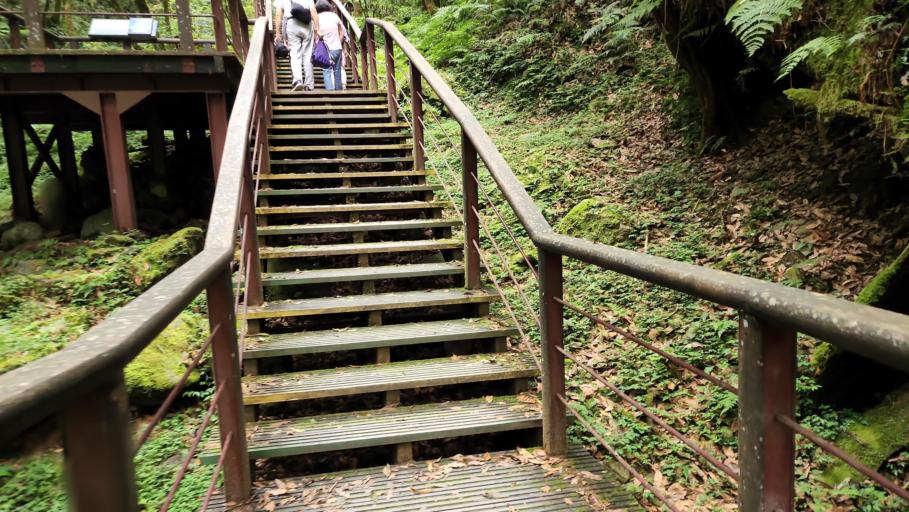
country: TW
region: Taiwan
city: Daxi
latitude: 24.7095
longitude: 121.4399
